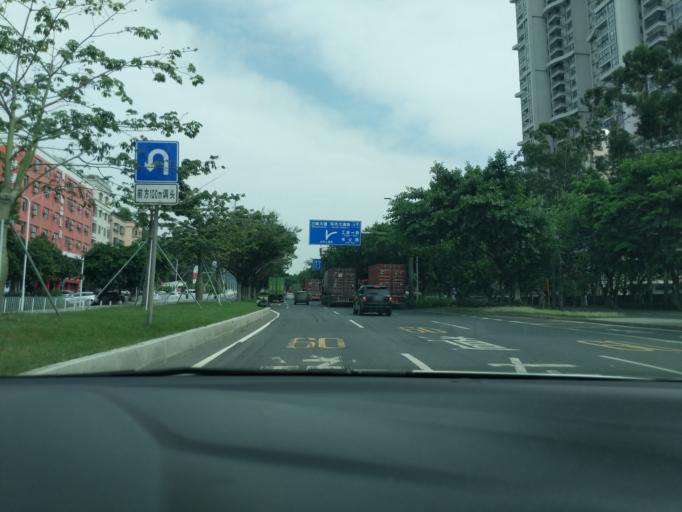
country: CN
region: Guangdong
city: Nansha
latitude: 22.7566
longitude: 113.5582
